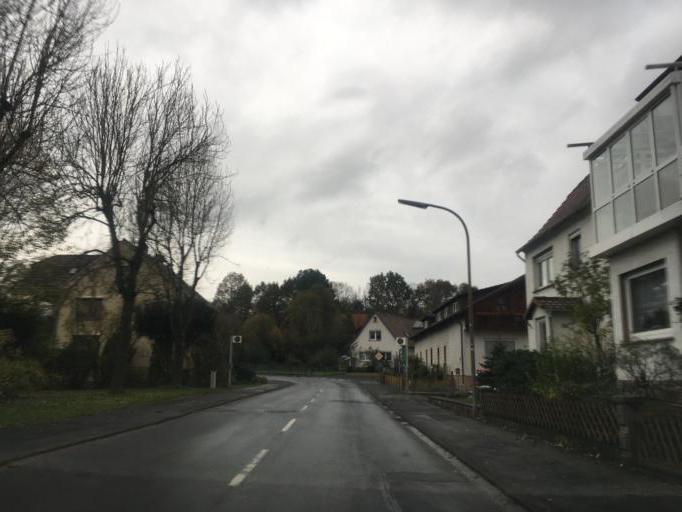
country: DE
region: Lower Saxony
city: Uslar
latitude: 51.6292
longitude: 9.6205
